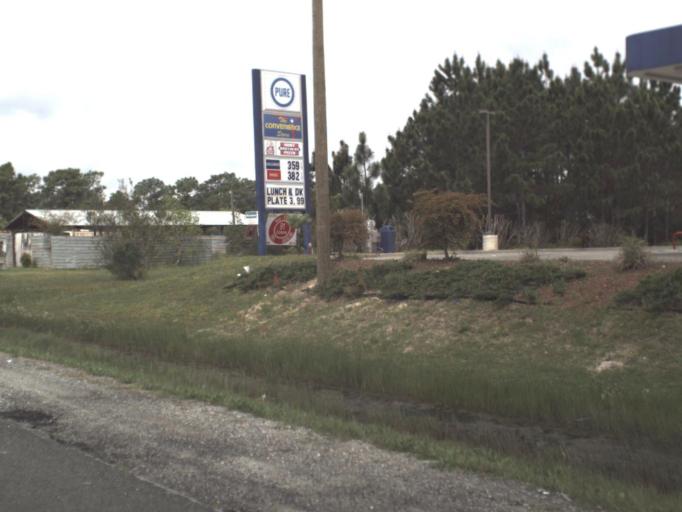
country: US
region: Florida
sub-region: Santa Rosa County
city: Woodlawn Beach
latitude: 30.4040
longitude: -86.9662
